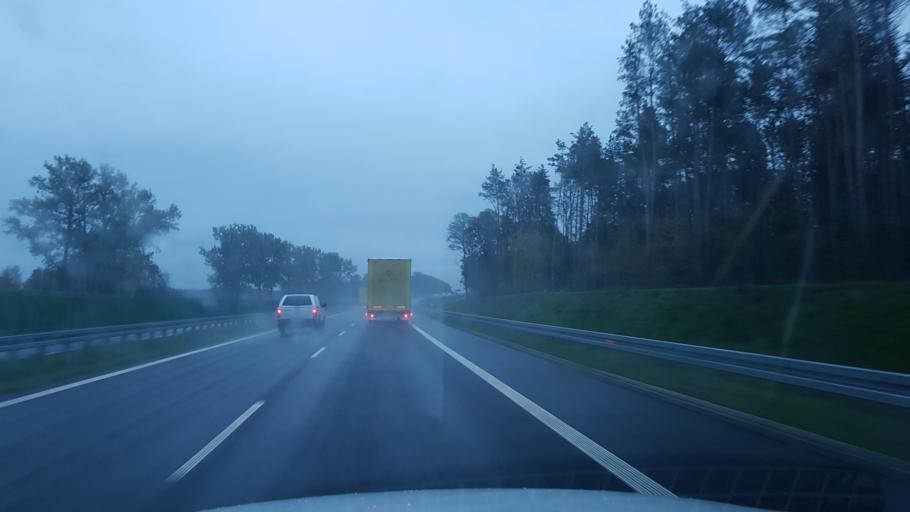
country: PL
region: West Pomeranian Voivodeship
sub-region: Powiat gryficki
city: Ploty
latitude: 53.8581
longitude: 15.3464
